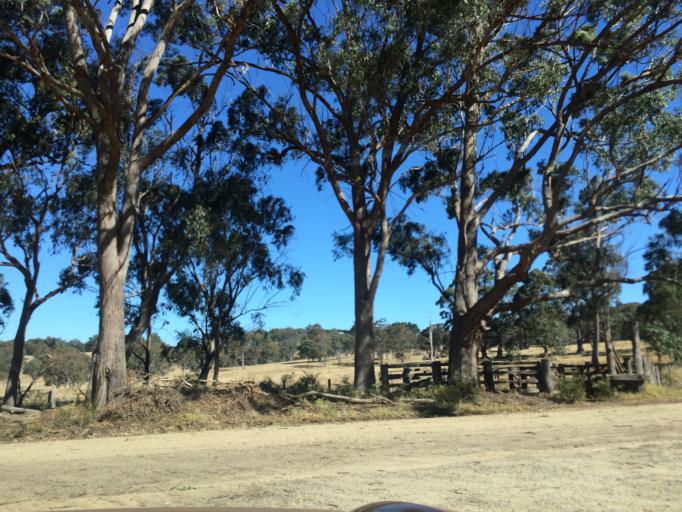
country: AU
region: Queensland
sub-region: Southern Downs
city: Stanthorpe
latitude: -28.6537
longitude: 152.0809
